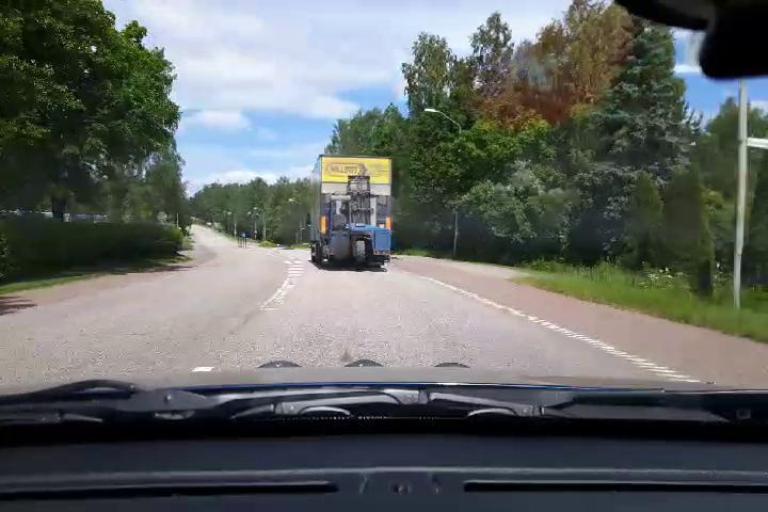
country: SE
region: Uppsala
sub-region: Osthammars Kommun
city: Bjorklinge
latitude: 60.0896
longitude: 17.5546
